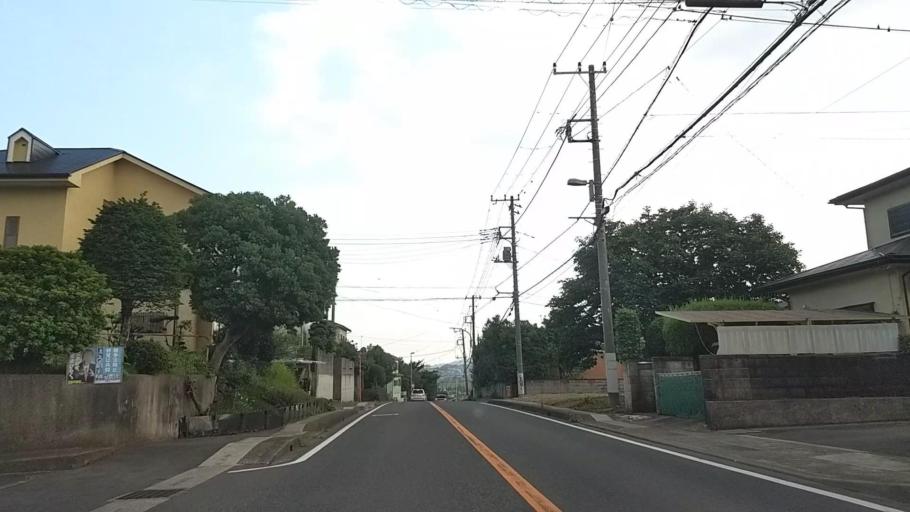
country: JP
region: Kanagawa
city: Isehara
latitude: 35.3767
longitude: 139.2999
